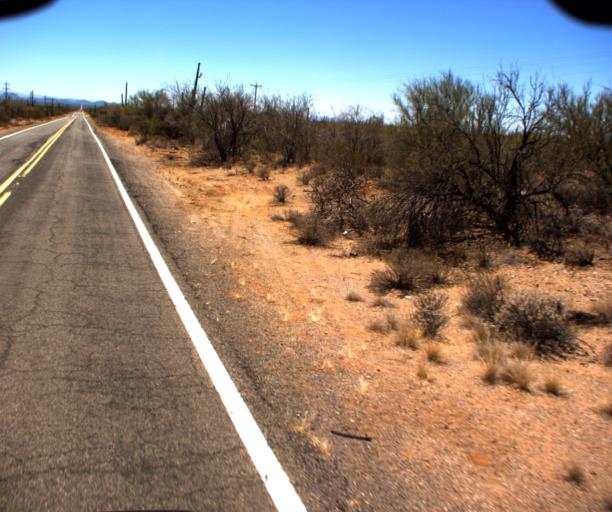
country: US
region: Arizona
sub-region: Pima County
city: Sells
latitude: 32.1388
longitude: -112.0967
